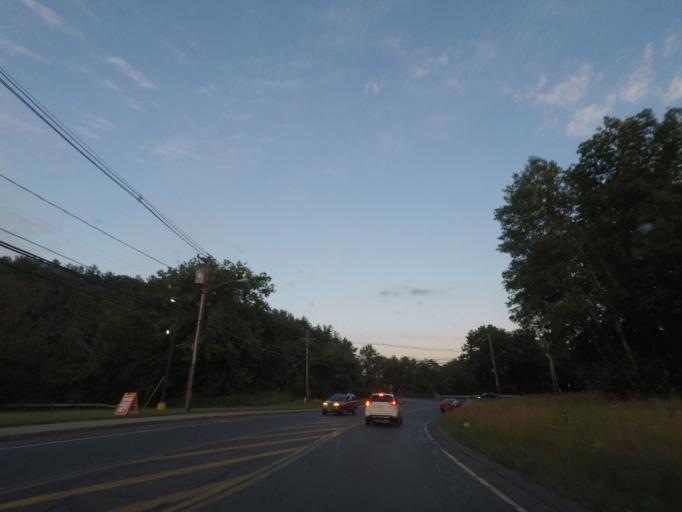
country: US
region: Massachusetts
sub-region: Worcester County
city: Southbridge
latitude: 42.0679
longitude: -72.0086
